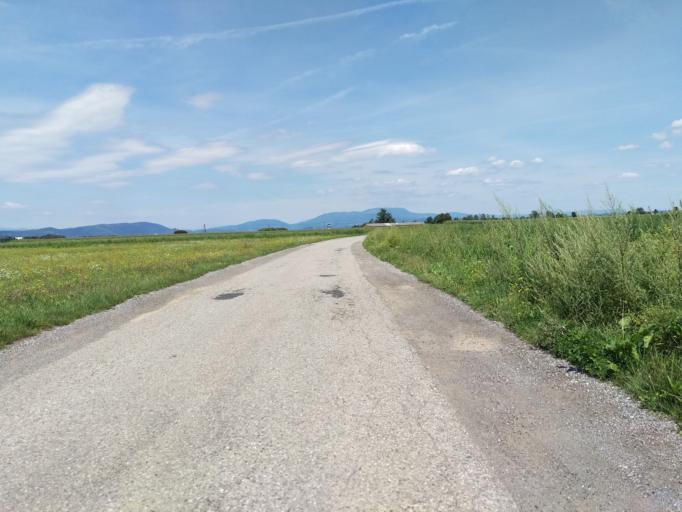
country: AT
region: Styria
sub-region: Politischer Bezirk Graz-Umgebung
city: Kalsdorf bei Graz
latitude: 46.9706
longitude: 15.4472
